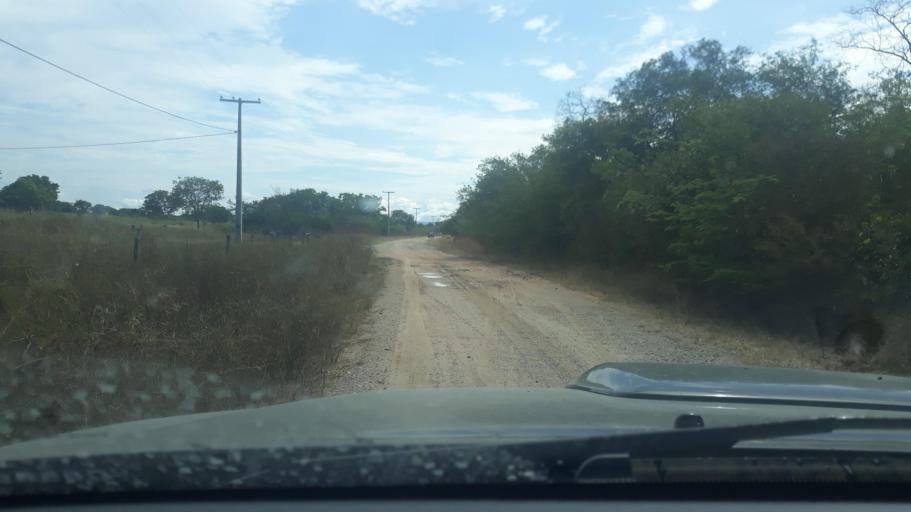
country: BR
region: Bahia
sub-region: Riacho De Santana
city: Riacho de Santana
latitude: -13.8749
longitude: -43.0204
